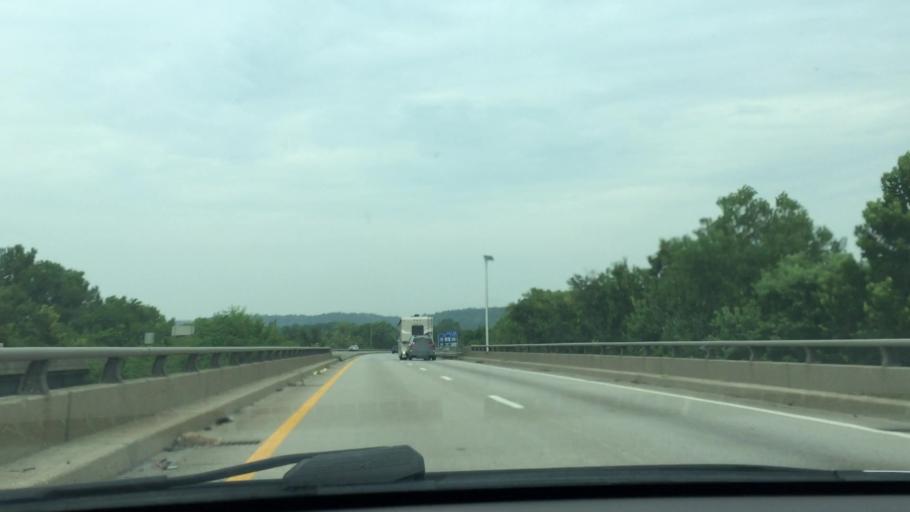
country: US
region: Kentucky
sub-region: Carroll County
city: Carrollton
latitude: 38.6436
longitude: -85.1241
